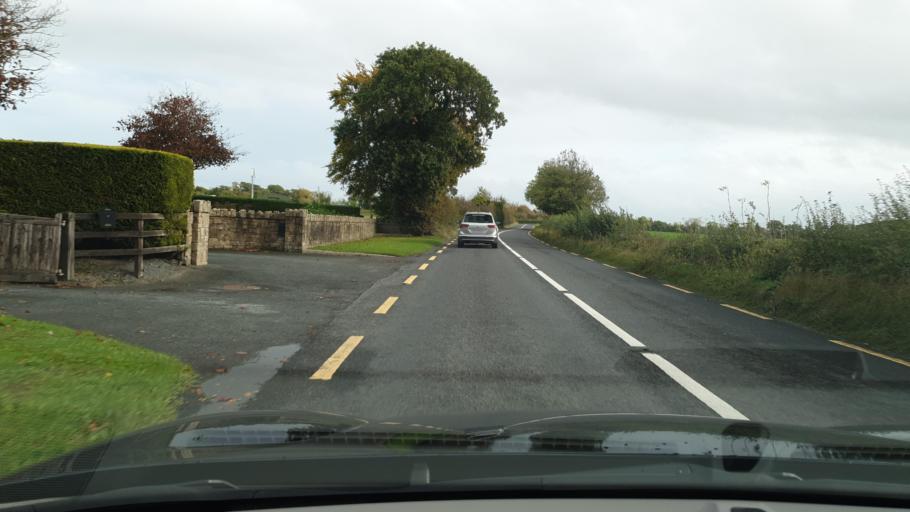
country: IE
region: Leinster
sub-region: An Mhi
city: Dunshaughlin
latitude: 53.5218
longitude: -6.5112
